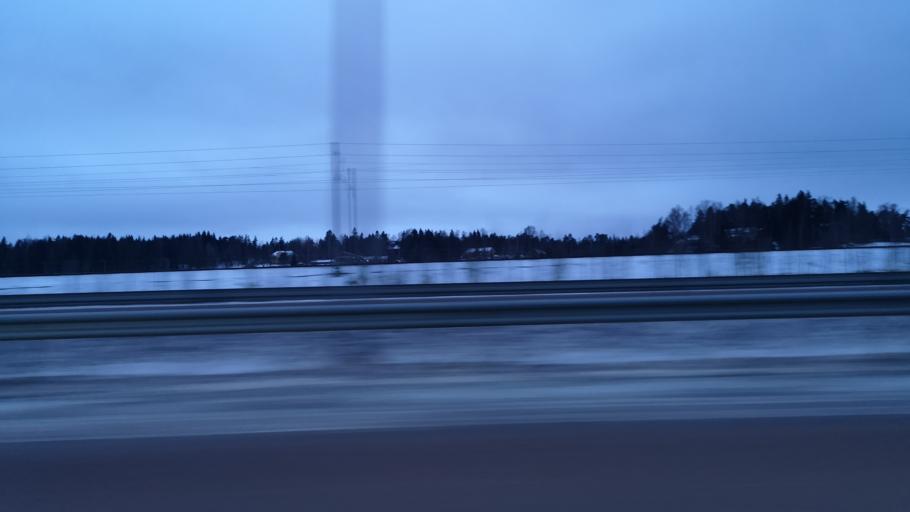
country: FI
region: Uusimaa
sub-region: Helsinki
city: Kirkkonummi
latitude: 60.1308
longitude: 24.4972
